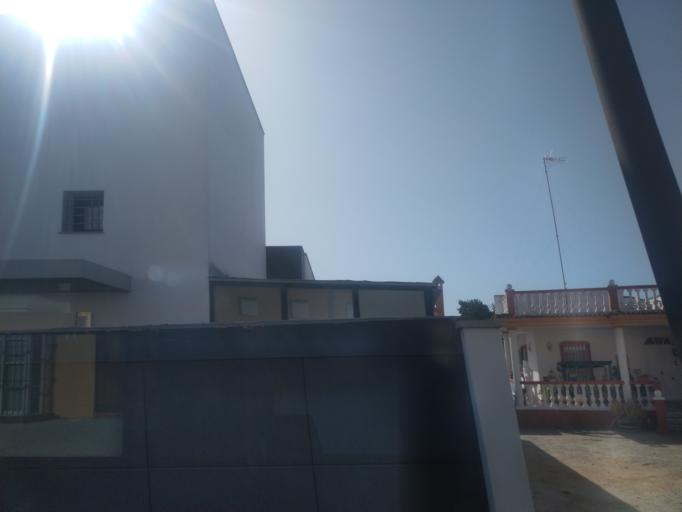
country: ES
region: Andalusia
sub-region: Provincia de Cadiz
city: San Fernando
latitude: 36.4540
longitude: -6.2109
